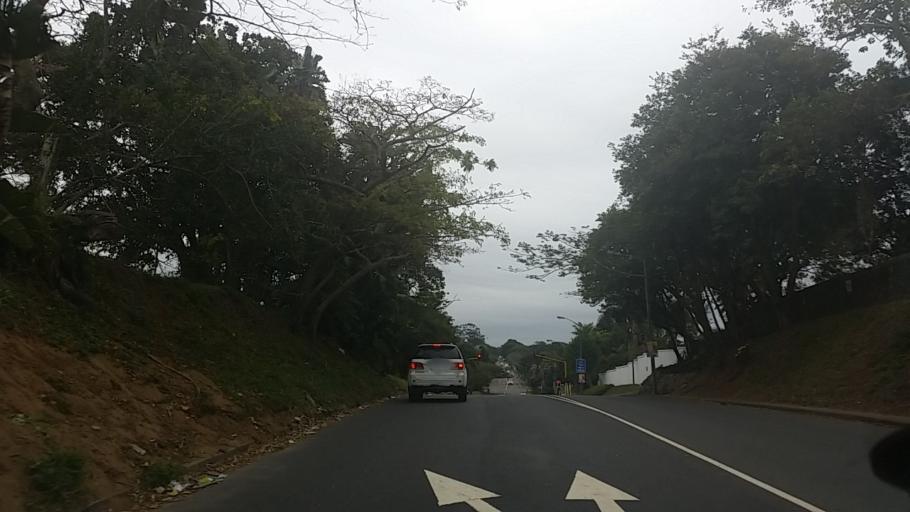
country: ZA
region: KwaZulu-Natal
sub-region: eThekwini Metropolitan Municipality
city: Berea
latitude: -29.8384
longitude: 30.9254
